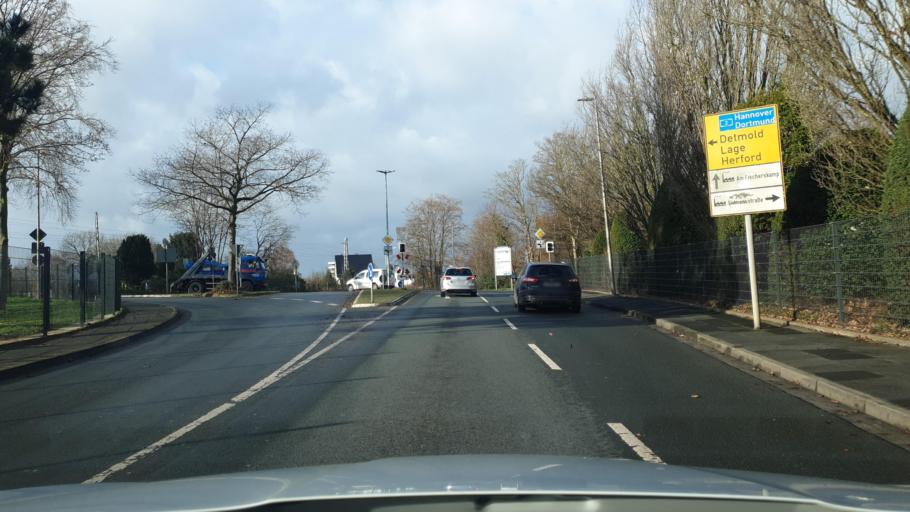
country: DE
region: North Rhine-Westphalia
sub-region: Regierungsbezirk Detmold
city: Bad Salzuflen
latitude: 52.0846
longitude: 8.7346
